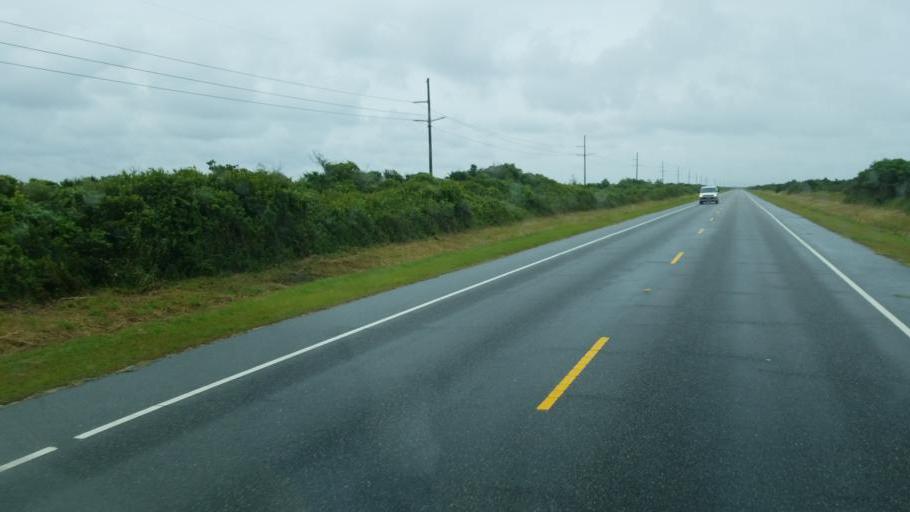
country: US
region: North Carolina
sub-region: Dare County
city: Buxton
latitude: 35.4546
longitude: -75.4848
